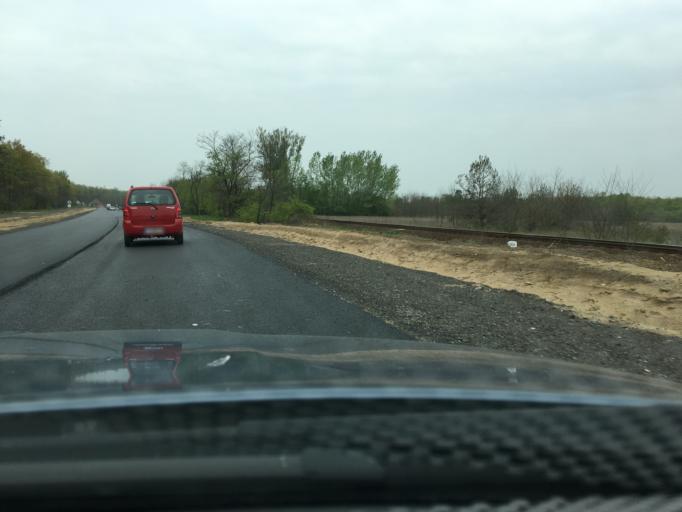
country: HU
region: Hajdu-Bihar
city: Hajdusamson
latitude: 47.6350
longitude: 21.7993
